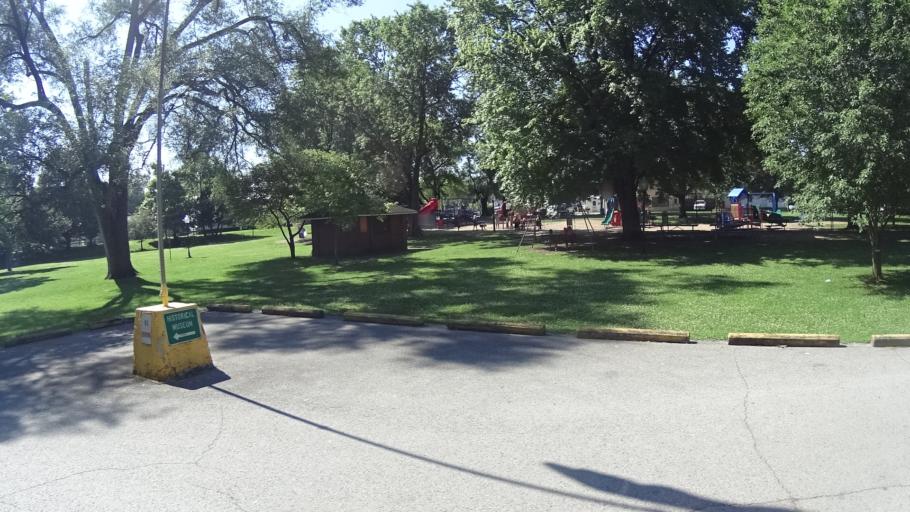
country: US
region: Indiana
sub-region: Madison County
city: Pendleton
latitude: 40.0046
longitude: -85.7450
